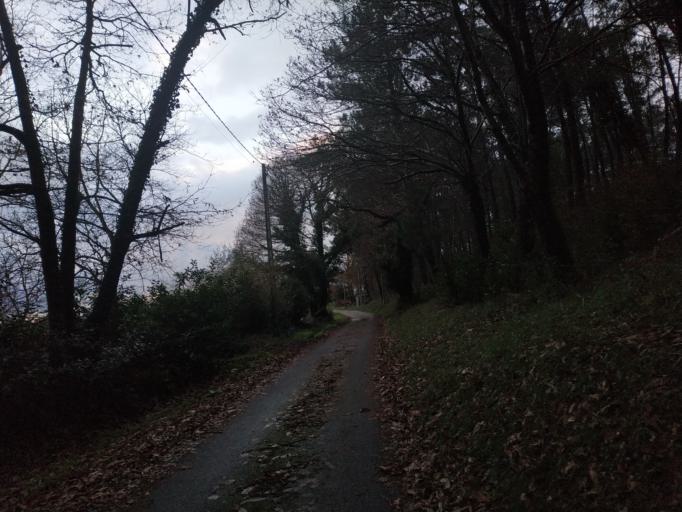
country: ES
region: Galicia
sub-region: Provincia de Pontevedra
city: Silleda
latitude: 42.7833
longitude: -8.1674
